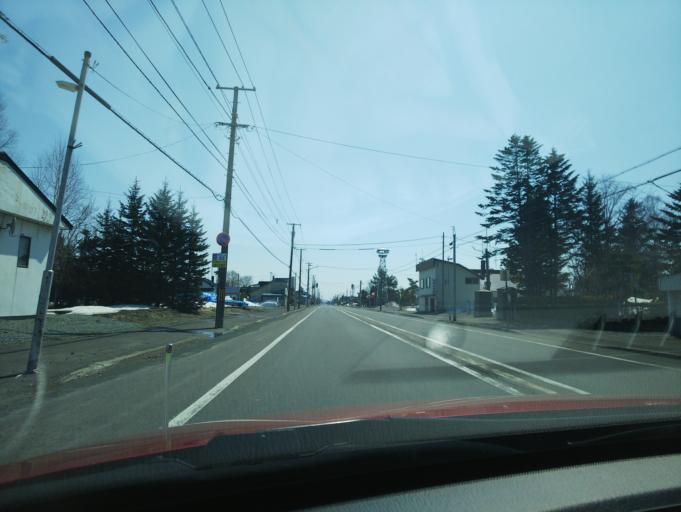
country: JP
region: Hokkaido
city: Nayoro
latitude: 44.2400
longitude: 142.3948
